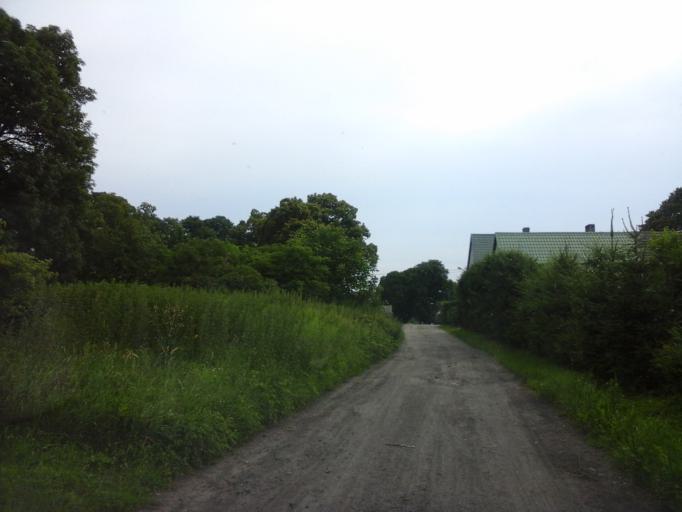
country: PL
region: West Pomeranian Voivodeship
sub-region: Powiat choszczenski
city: Recz
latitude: 53.2203
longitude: 15.6080
